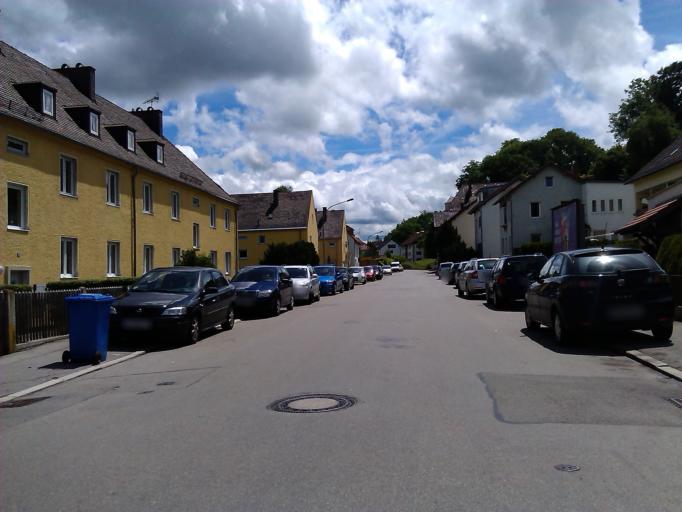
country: DE
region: Bavaria
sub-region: Swabia
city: Kaufbeuren
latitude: 47.8742
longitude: 10.6223
